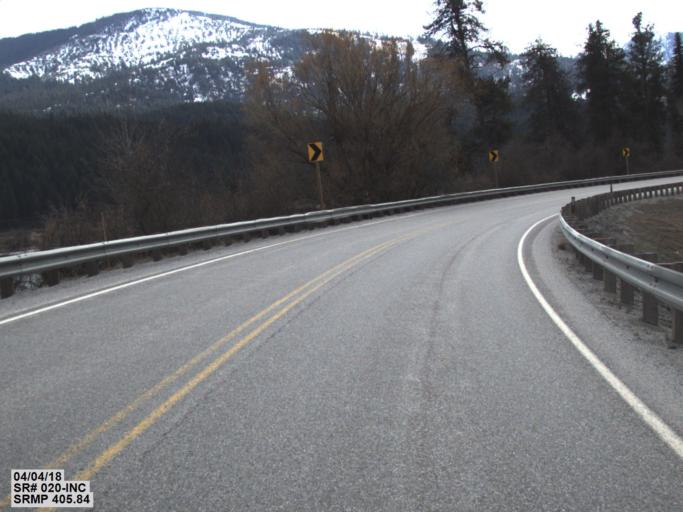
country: US
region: Washington
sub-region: Pend Oreille County
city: Newport
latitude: 48.4998
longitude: -117.2694
